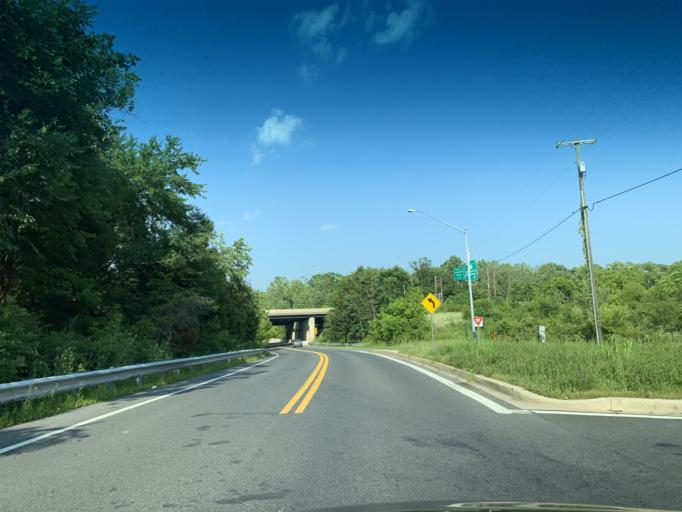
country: US
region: Maryland
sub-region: Frederick County
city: Green Valley
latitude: 39.2774
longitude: -77.3249
